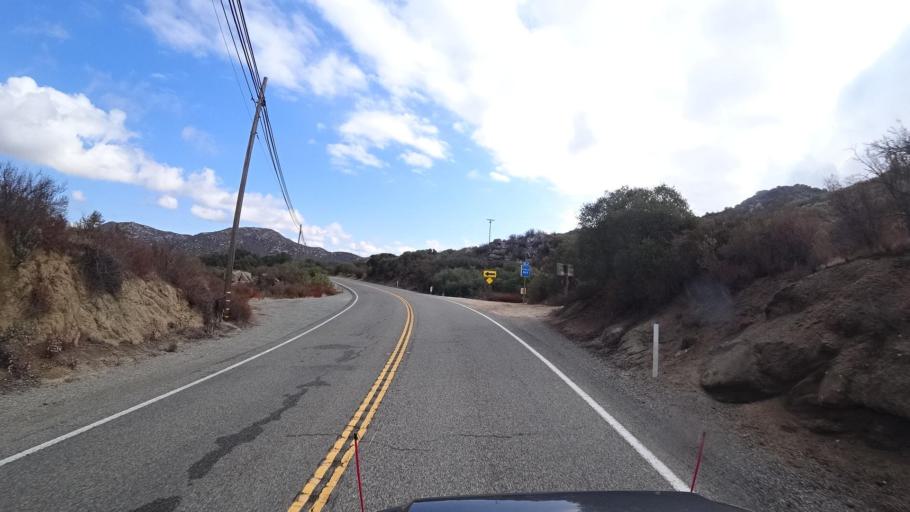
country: US
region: California
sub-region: San Diego County
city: Campo
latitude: 32.6020
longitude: -116.4894
